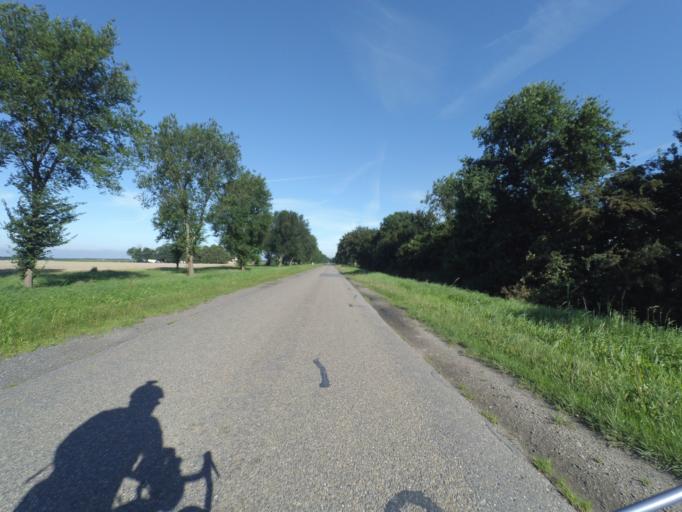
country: NL
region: Flevoland
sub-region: Gemeente Zeewolde
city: Zeewolde
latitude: 52.3839
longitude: 5.4970
